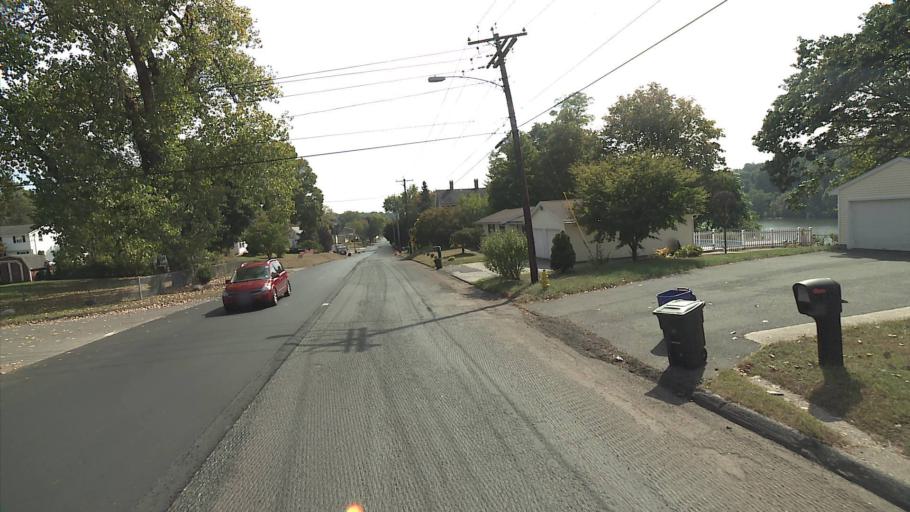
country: US
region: Connecticut
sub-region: Fairfield County
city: Shelton
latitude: 41.3306
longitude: -73.1095
